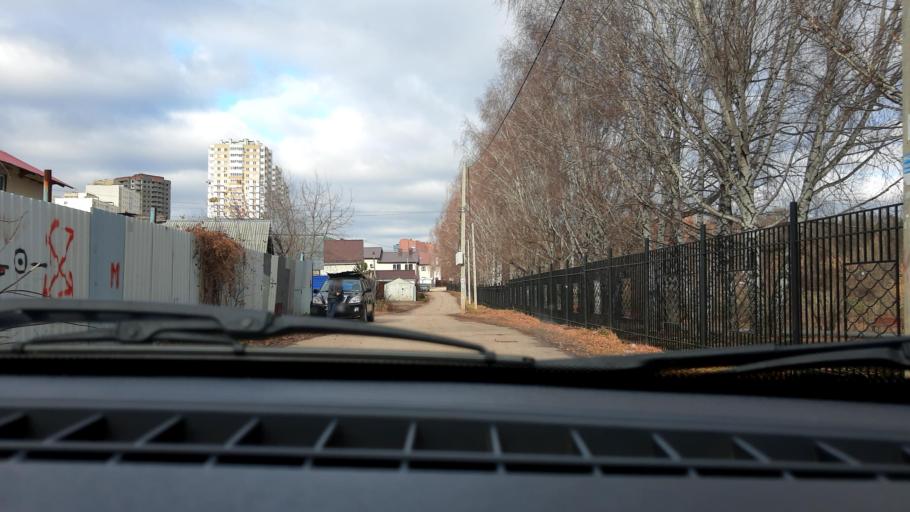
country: RU
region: Bashkortostan
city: Mikhaylovka
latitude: 54.7873
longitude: 55.8759
